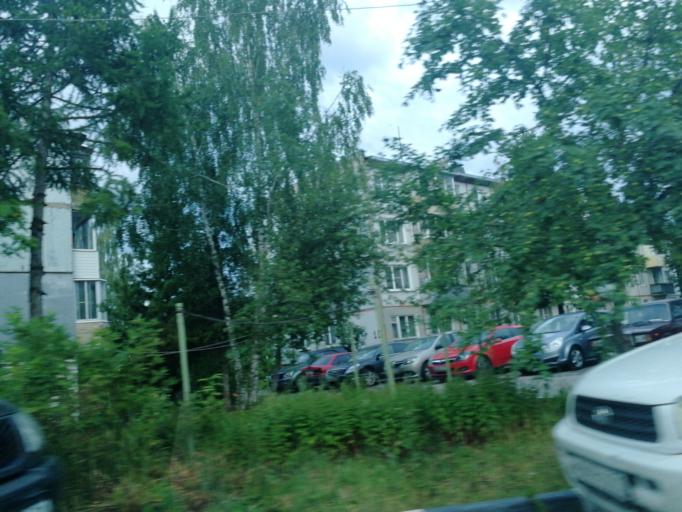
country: RU
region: Tula
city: Kosaya Gora
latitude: 54.1648
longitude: 37.4706
